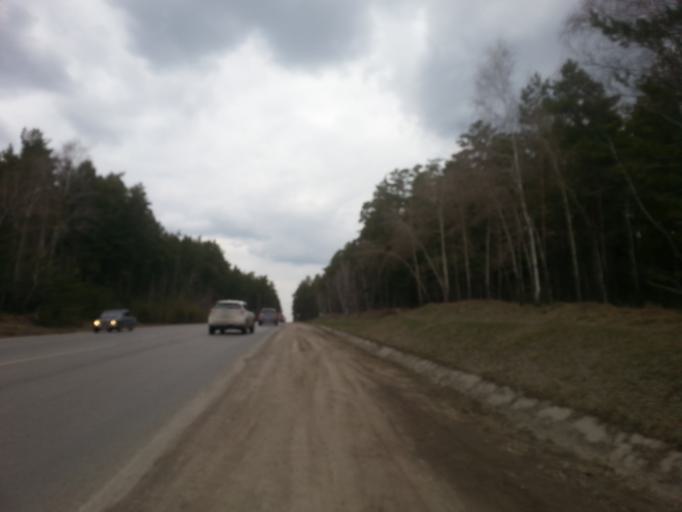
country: RU
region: Altai Krai
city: Yuzhnyy
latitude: 53.2693
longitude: 83.7257
